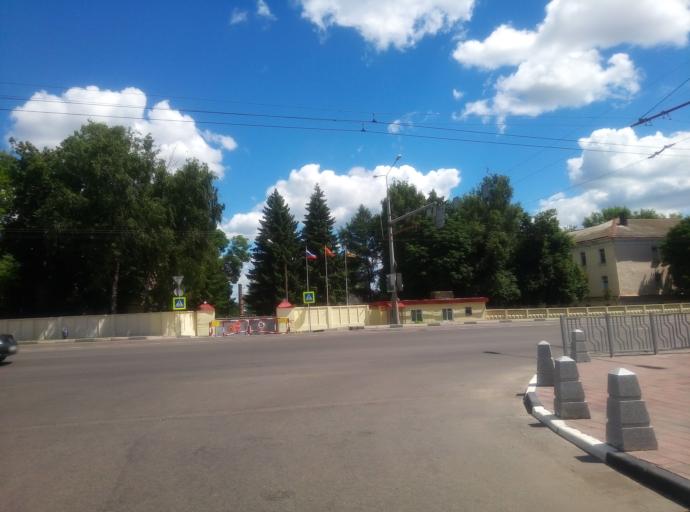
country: RU
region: Kursk
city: Kursk
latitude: 51.7632
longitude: 36.1845
